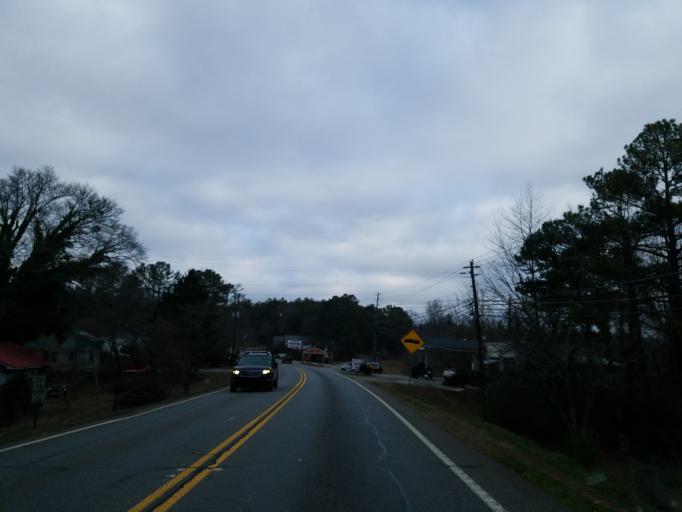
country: US
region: Georgia
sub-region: Cherokee County
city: Canton
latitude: 34.2606
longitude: -84.4934
